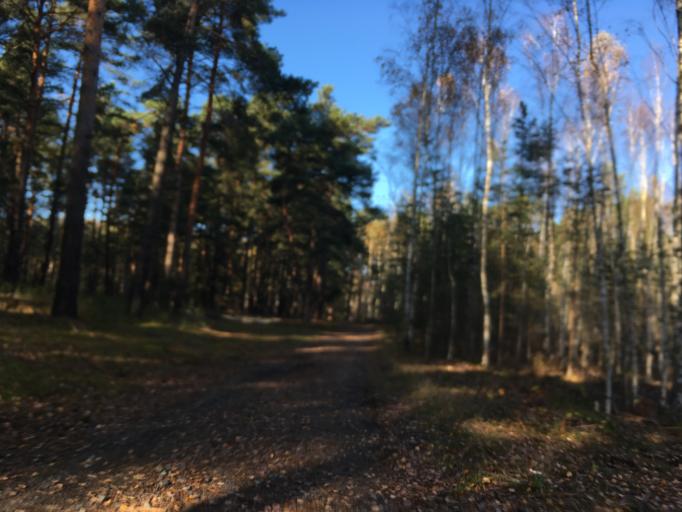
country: DE
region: Brandenburg
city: Wendisch Rietz
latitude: 52.1844
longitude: 13.9974
